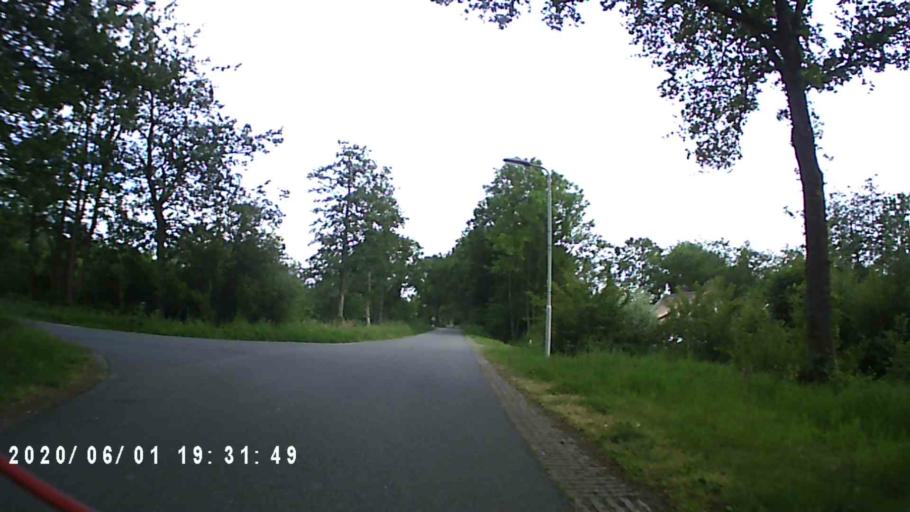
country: NL
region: Friesland
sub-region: Gemeente Achtkarspelen
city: Augustinusga
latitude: 53.2138
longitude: 6.1574
